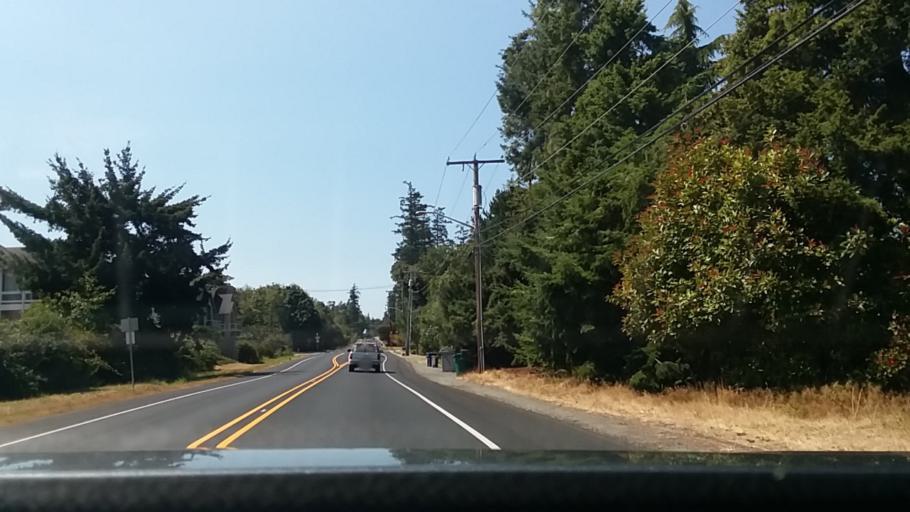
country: US
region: Washington
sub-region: Skagit County
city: Anacortes
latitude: 48.5091
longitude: -122.6501
